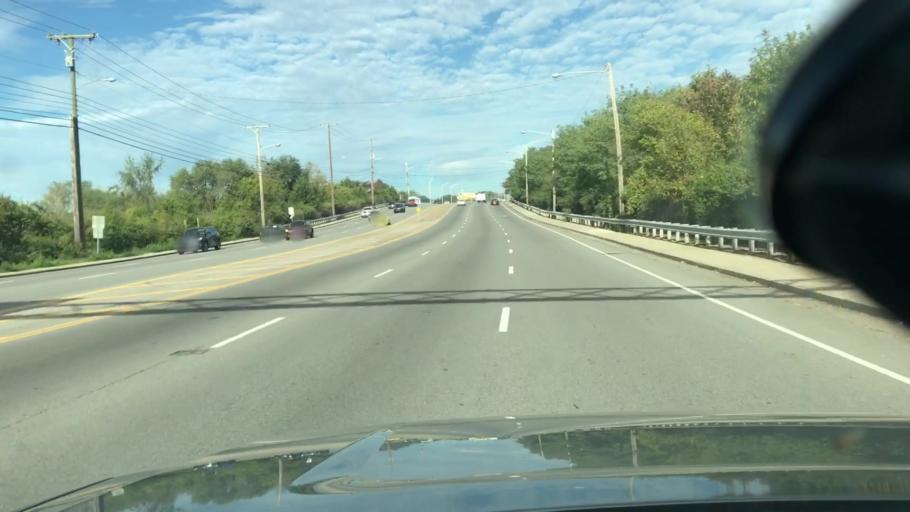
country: US
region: Tennessee
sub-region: Davidson County
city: Nashville
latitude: 36.1893
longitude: -86.8236
